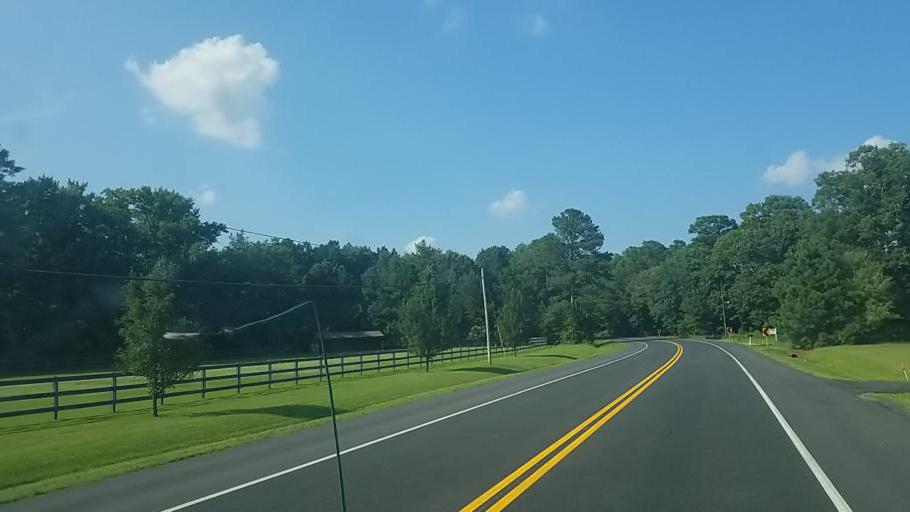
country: US
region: Maryland
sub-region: Worcester County
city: Berlin
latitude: 38.3694
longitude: -75.1990
